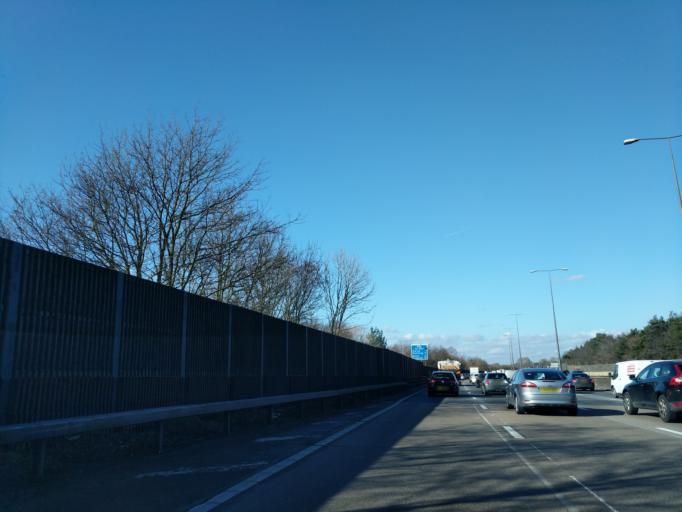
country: GB
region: England
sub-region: Surrey
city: Byfleet
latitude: 51.3276
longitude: -0.4758
